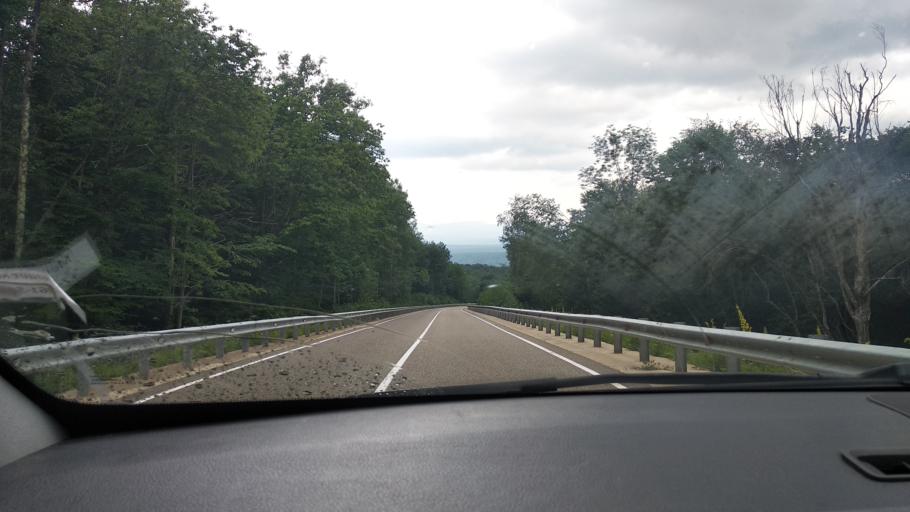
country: RU
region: Adygeya
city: Kamennomostskiy
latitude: 44.2552
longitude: 39.9644
